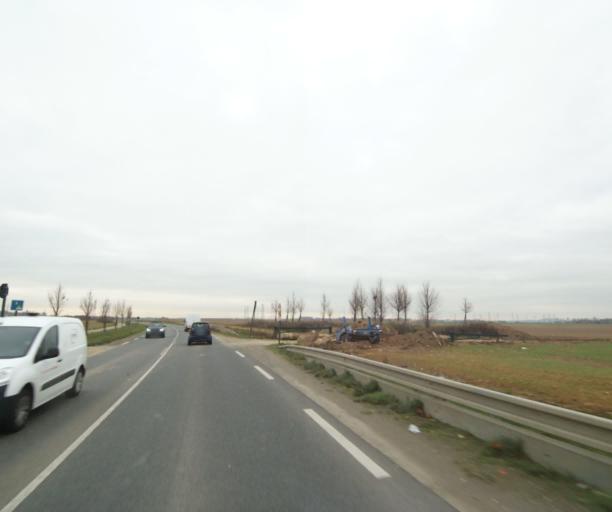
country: FR
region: Ile-de-France
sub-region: Departement du Val-d'Oise
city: Villiers-le-Bel
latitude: 49.0088
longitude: 2.4238
